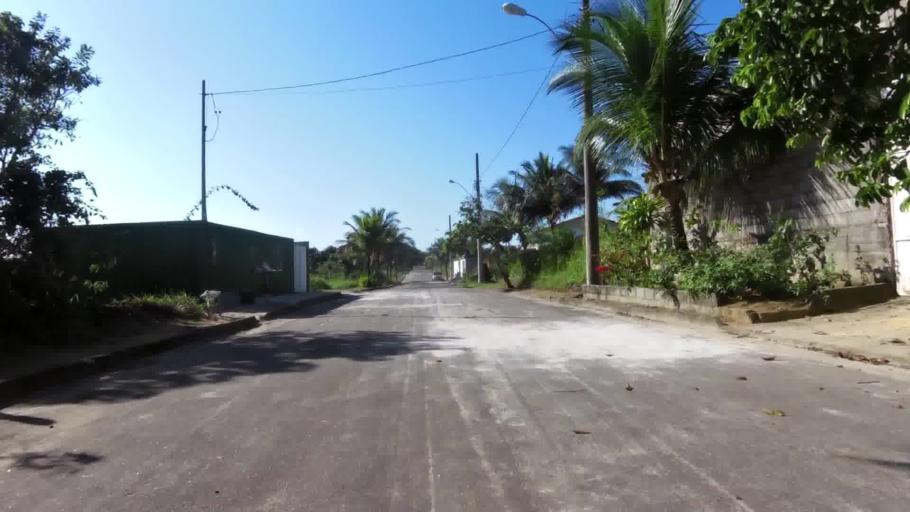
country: BR
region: Espirito Santo
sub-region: Guarapari
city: Guarapari
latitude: -20.7456
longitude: -40.5597
